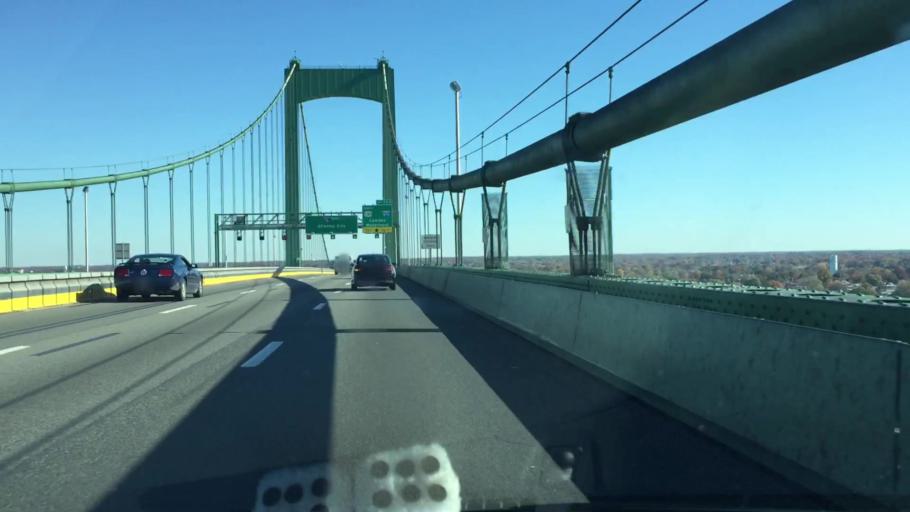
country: US
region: New Jersey
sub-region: Camden County
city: Gloucester City
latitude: 39.9051
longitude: -75.1291
